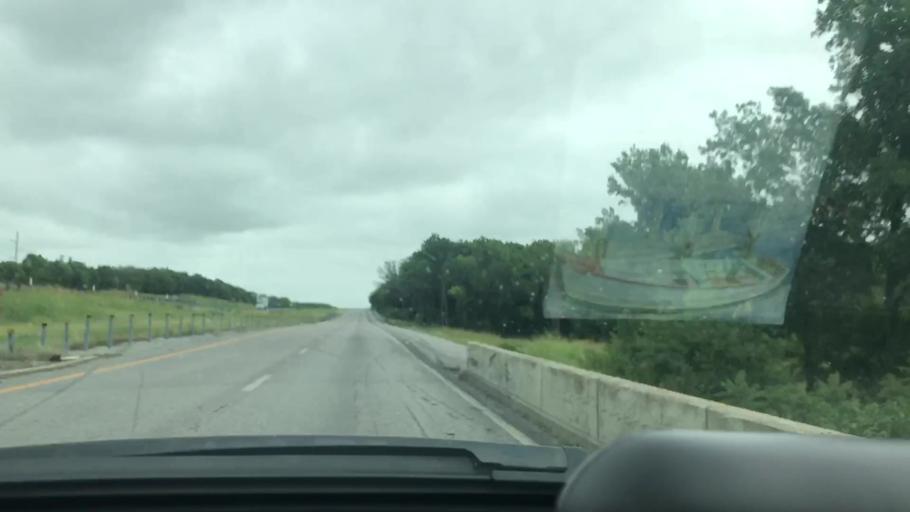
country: US
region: Oklahoma
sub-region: Coal County
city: Coalgate
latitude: 34.6263
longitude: -95.9602
